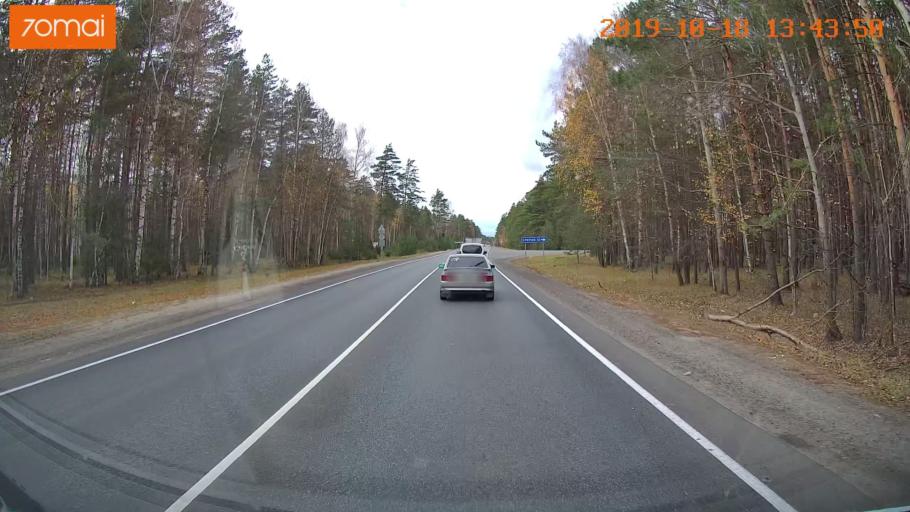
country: RU
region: Rjazan
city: Solotcha
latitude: 54.9330
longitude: 39.9714
